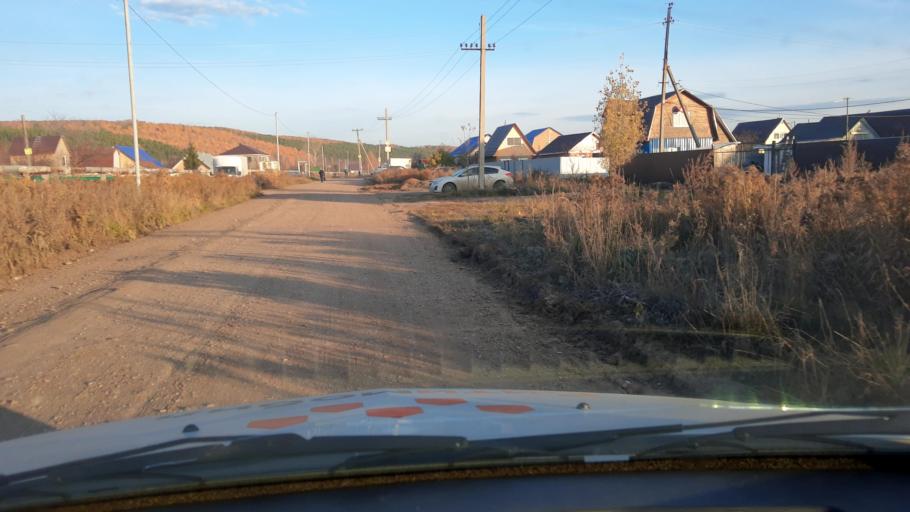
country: RU
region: Bashkortostan
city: Ufa
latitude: 54.8130
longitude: 56.1559
